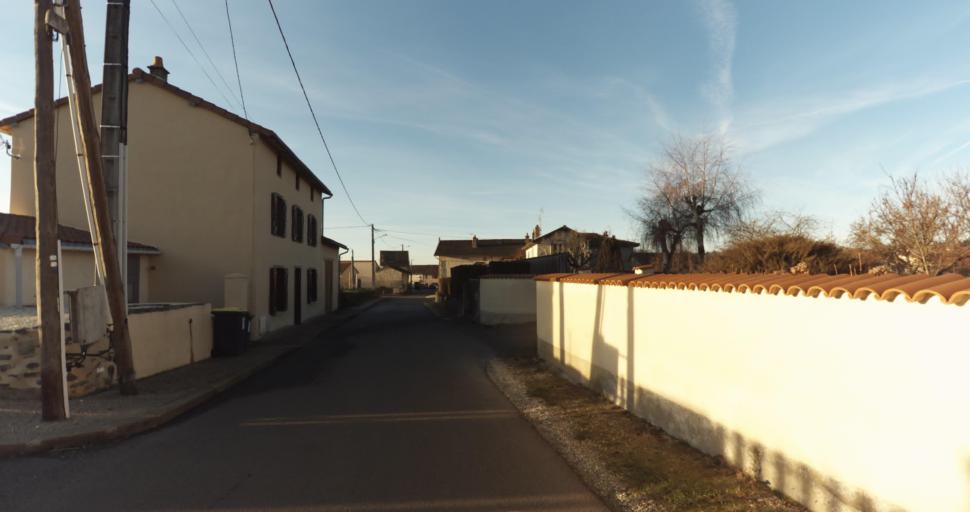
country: FR
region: Limousin
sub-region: Departement de la Haute-Vienne
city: Aixe-sur-Vienne
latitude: 45.7929
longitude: 1.1448
